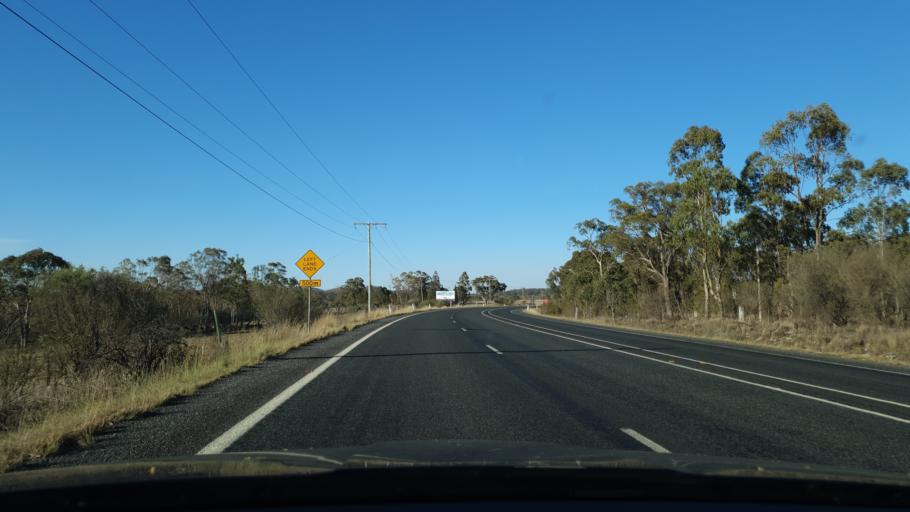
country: AU
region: Queensland
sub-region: Southern Downs
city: Stanthorpe
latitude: -28.6926
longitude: 151.9075
